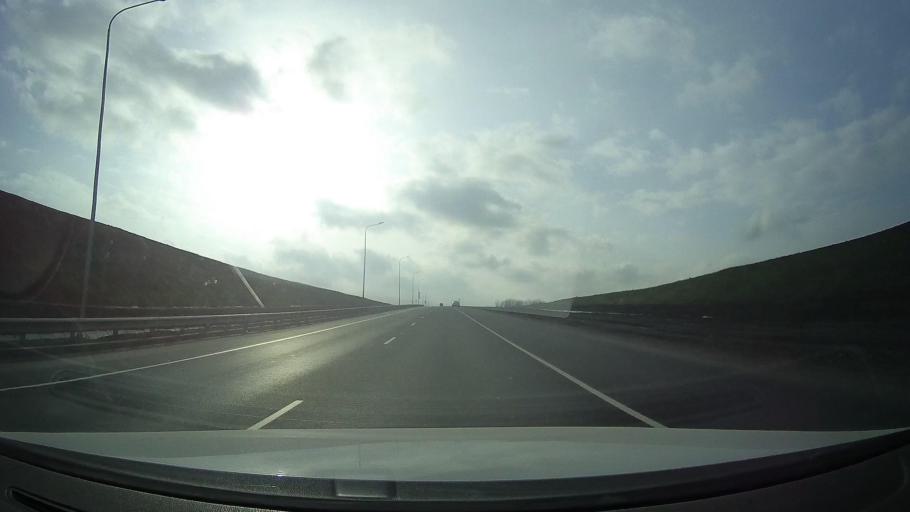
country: RU
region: Rostov
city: Grushevskaya
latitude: 47.4316
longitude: 39.8682
